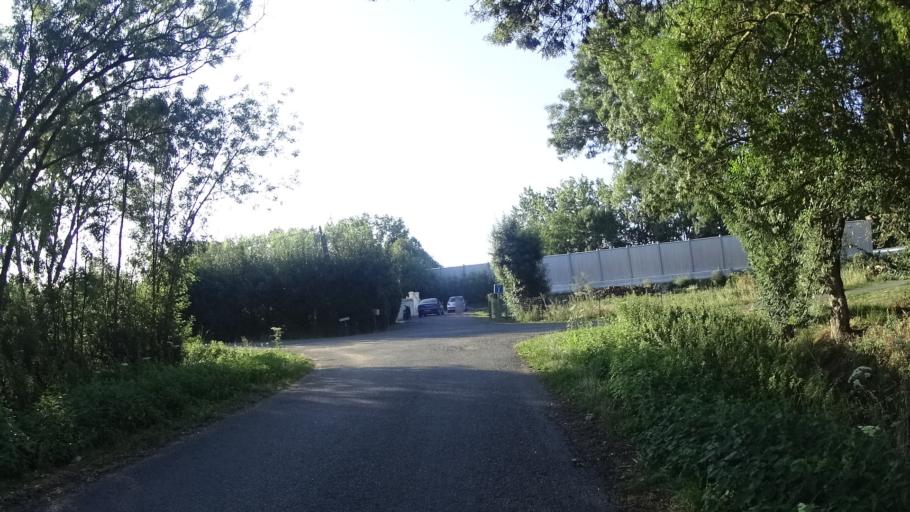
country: FR
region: Pays de la Loire
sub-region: Departement de Maine-et-Loire
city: Saumur
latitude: 47.2840
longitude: -0.0574
